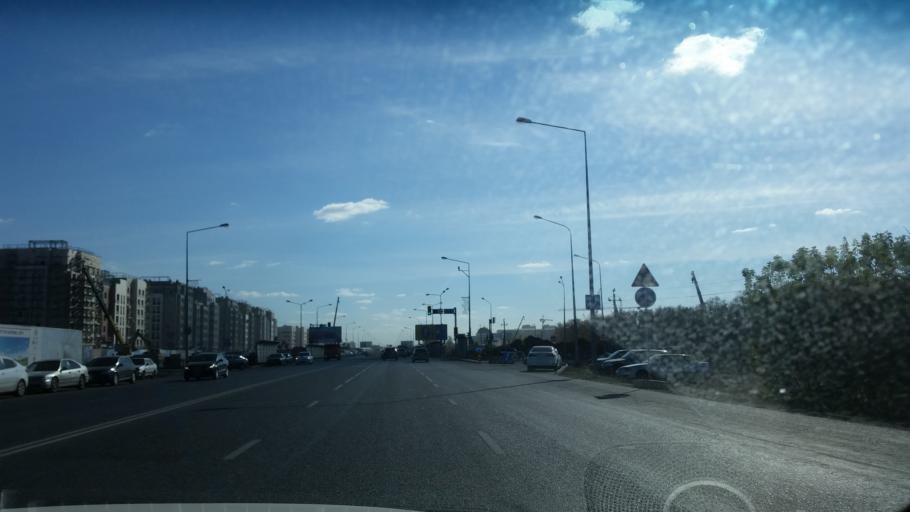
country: KZ
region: Astana Qalasy
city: Astana
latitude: 51.0998
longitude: 71.4063
